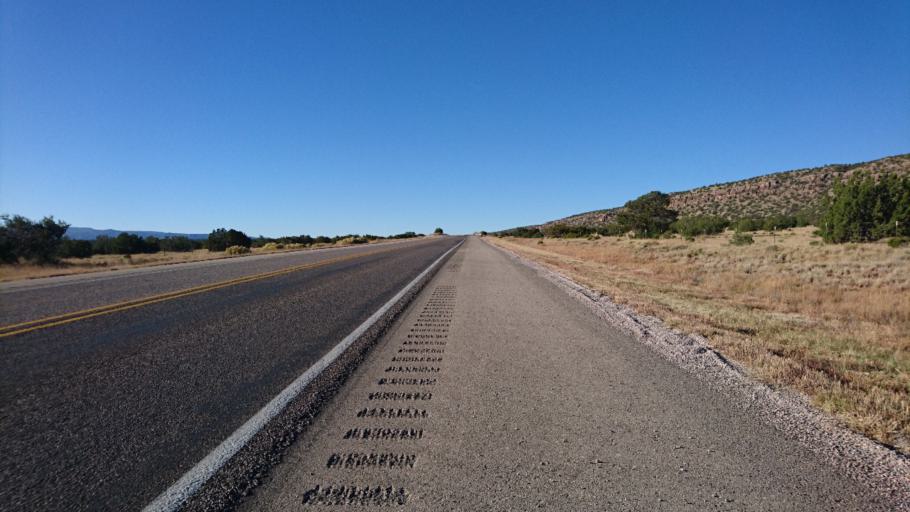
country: US
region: New Mexico
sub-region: Cibola County
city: Grants
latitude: 34.9994
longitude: -107.8960
